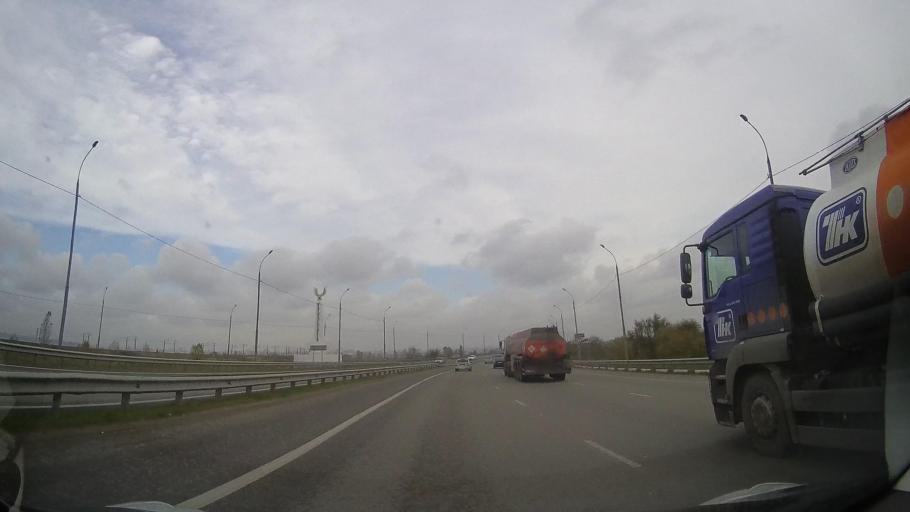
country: RU
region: Rostov
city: Bataysk
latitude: 47.1618
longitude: 39.7410
